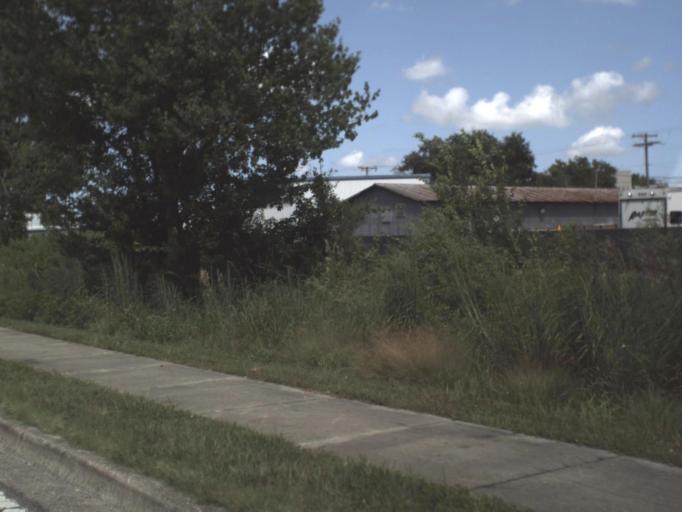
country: US
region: Florida
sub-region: Pinellas County
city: Oldsmar
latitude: 28.0381
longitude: -82.6700
